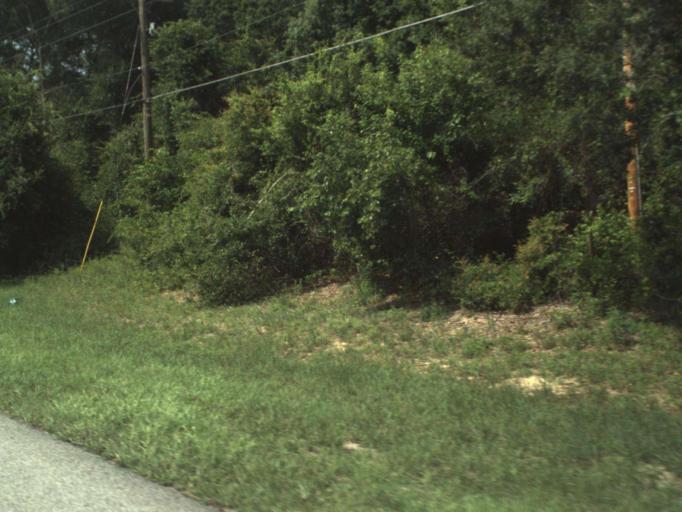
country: US
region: Florida
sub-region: Sumter County
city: Lake Panasoffkee
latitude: 28.7785
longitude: -82.0671
